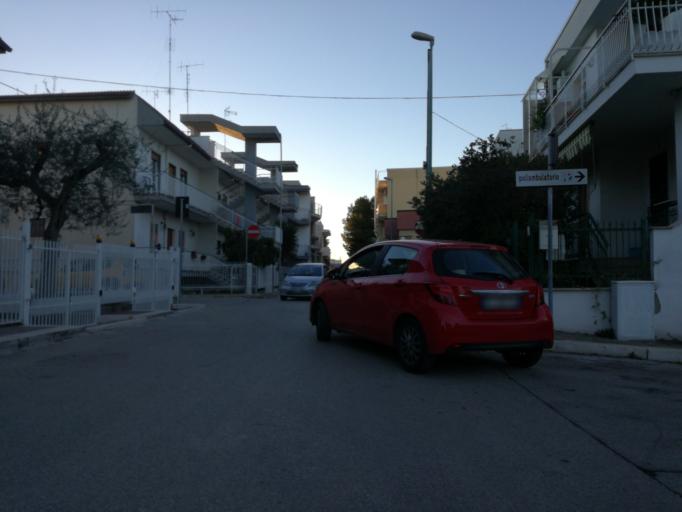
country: IT
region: Apulia
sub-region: Provincia di Bari
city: Adelfia
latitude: 41.0002
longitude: 16.8786
